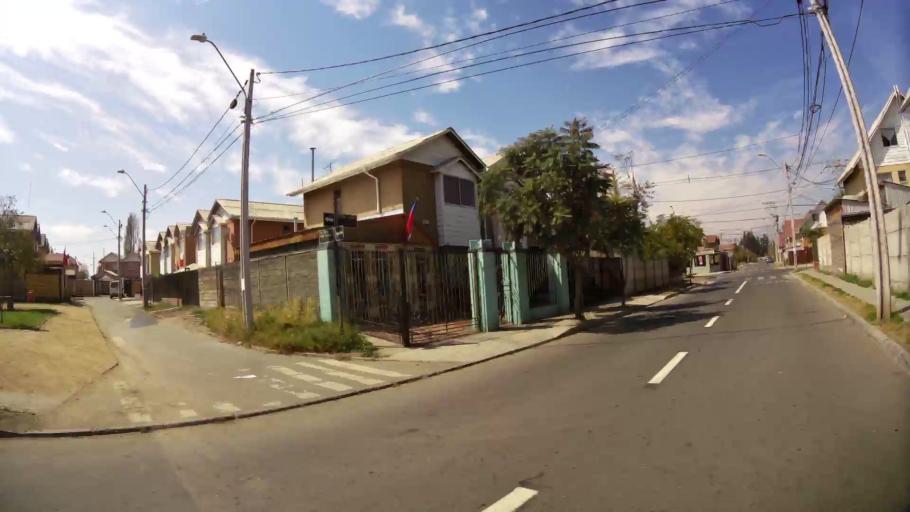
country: CL
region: Santiago Metropolitan
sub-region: Provincia de Talagante
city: Talagante
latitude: -33.6636
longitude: -70.9150
